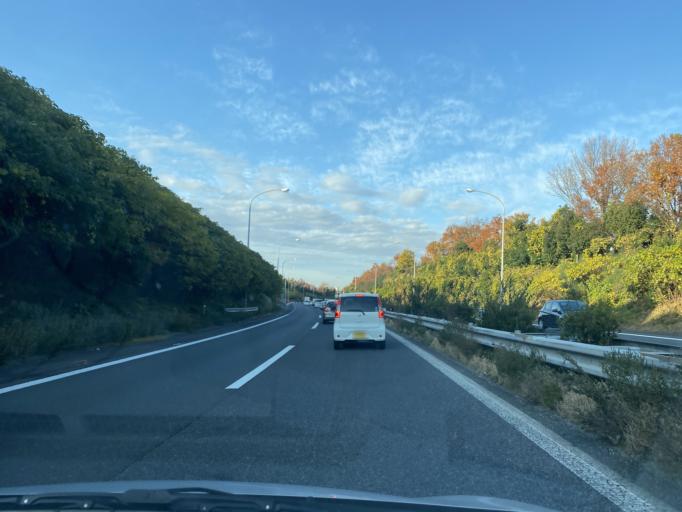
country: JP
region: Osaka
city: Izumi
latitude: 34.4493
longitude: 135.4453
